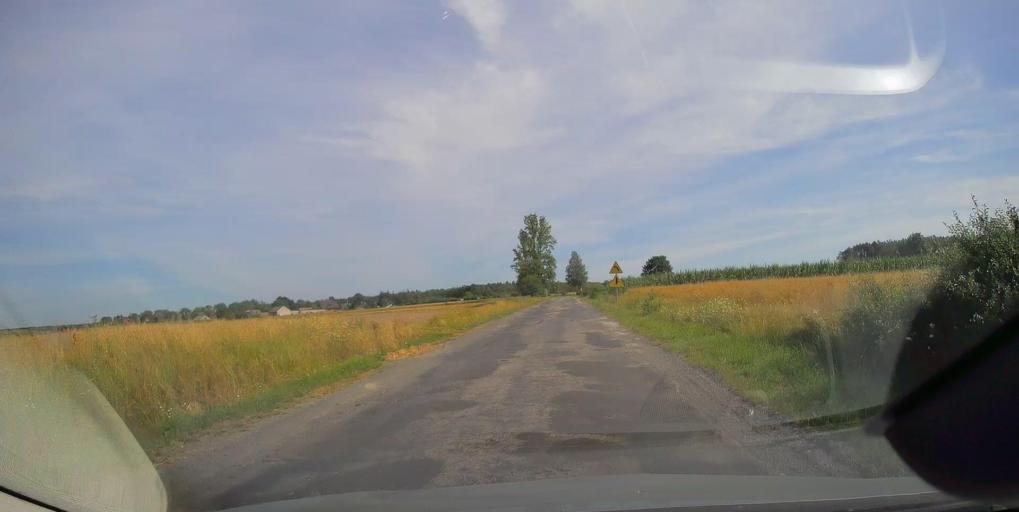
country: PL
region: Lodz Voivodeship
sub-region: Powiat opoczynski
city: Mniszkow
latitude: 51.4136
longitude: 20.0346
